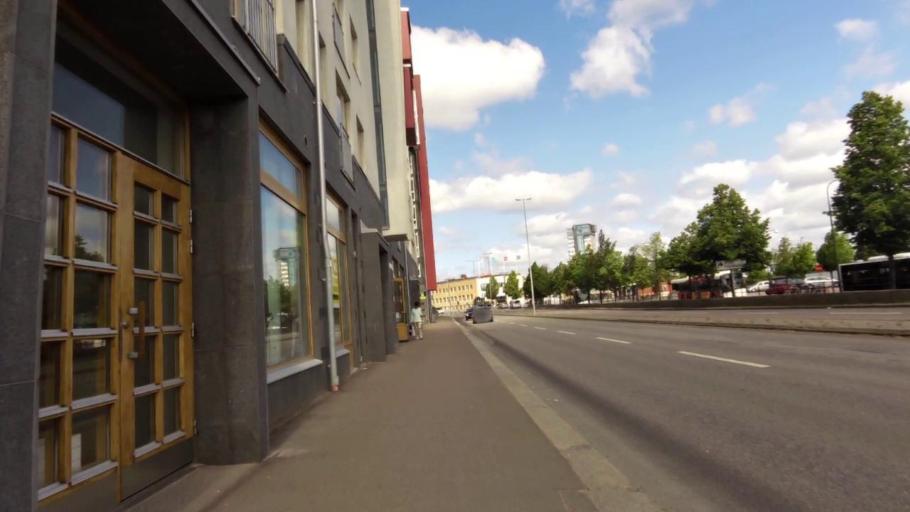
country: SE
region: OEstergoetland
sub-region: Linkopings Kommun
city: Linkoping
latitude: 58.4185
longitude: 15.6200
